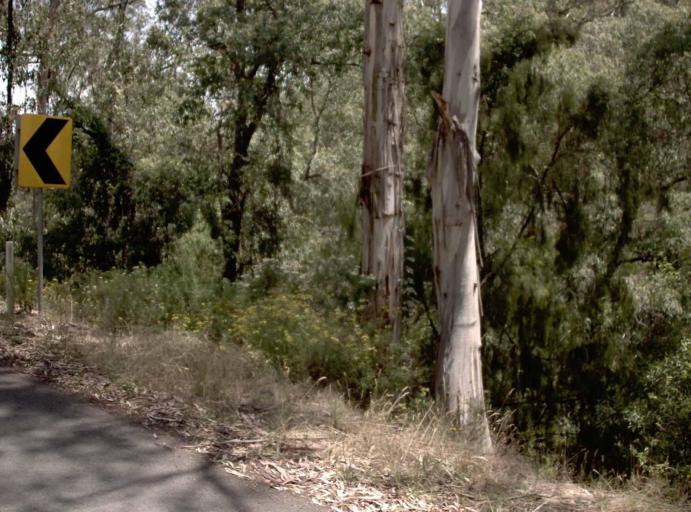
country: AU
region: Victoria
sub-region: Latrobe
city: Traralgon
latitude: -37.9519
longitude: 146.4346
